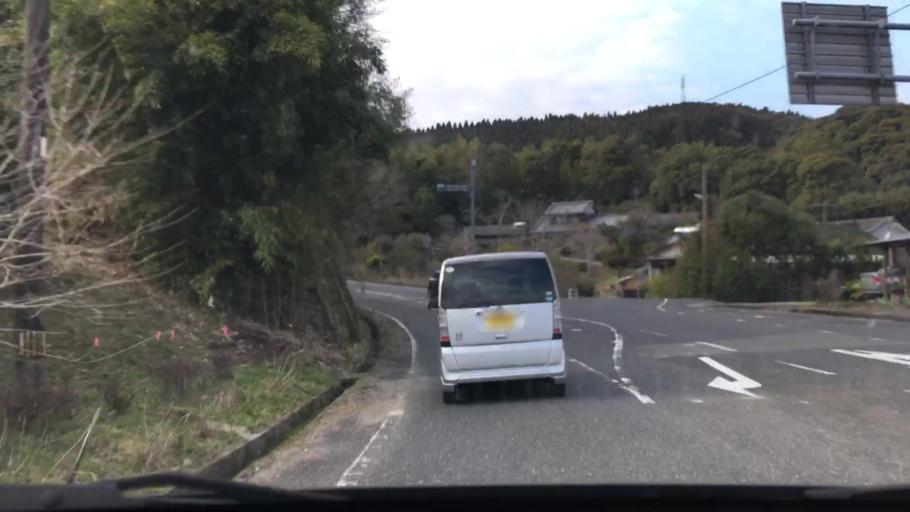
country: JP
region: Miyazaki
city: Nichinan
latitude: 31.6297
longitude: 131.3412
